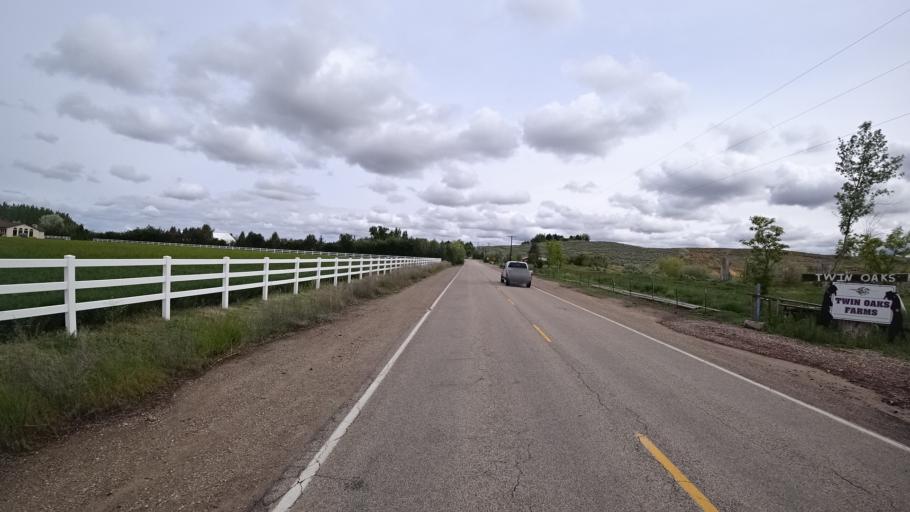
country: US
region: Idaho
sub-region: Ada County
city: Eagle
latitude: 43.7296
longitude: -116.3544
